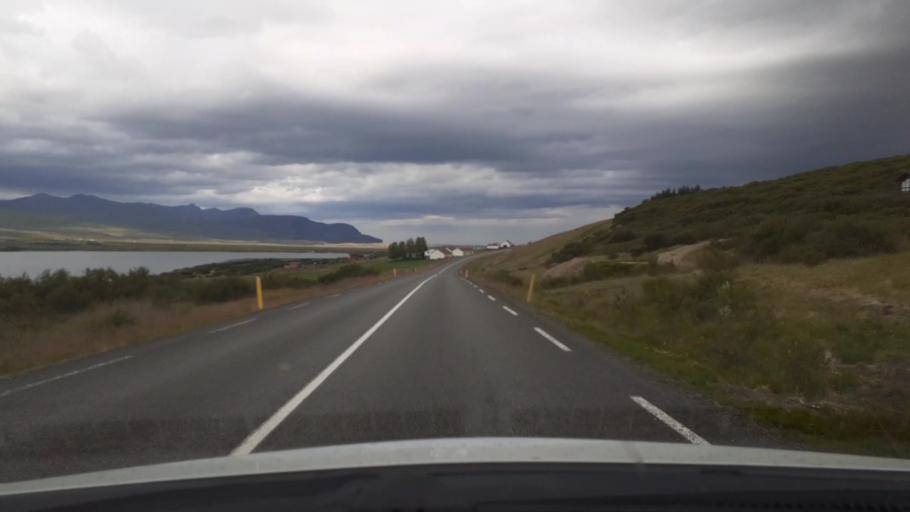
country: IS
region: West
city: Borgarnes
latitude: 64.5430
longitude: -21.5681
